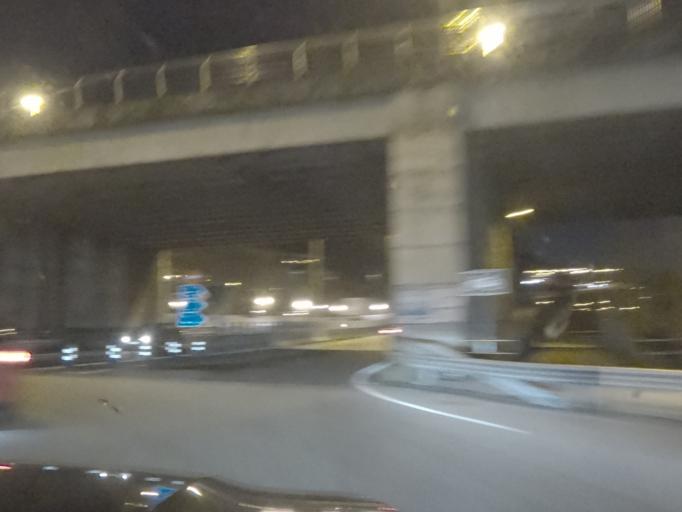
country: ES
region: Galicia
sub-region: Provincia de Ourense
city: Ourense
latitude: 42.3450
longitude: -7.8755
